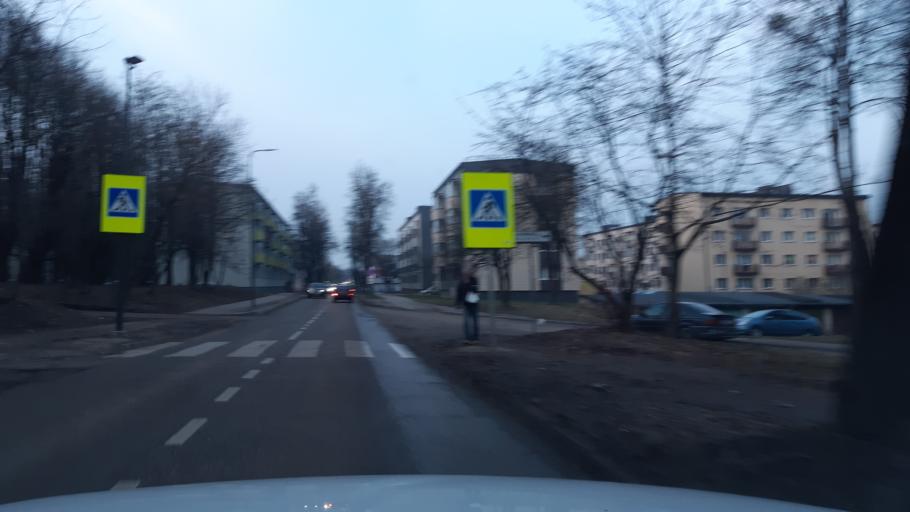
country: LT
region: Kauno apskritis
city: Dainava (Kaunas)
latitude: 54.8987
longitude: 23.9740
